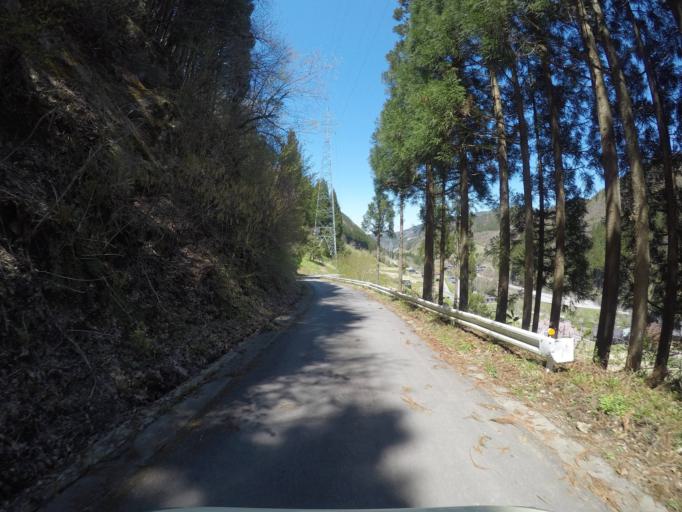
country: JP
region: Gifu
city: Takayama
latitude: 36.1691
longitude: 137.4335
